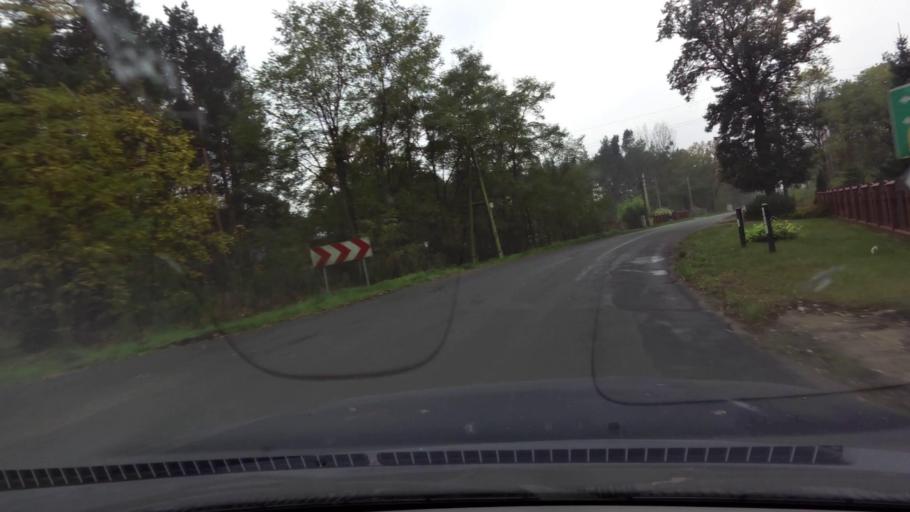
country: PL
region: West Pomeranian Voivodeship
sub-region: Powiat goleniowski
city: Goleniow
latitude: 53.5107
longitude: 14.7407
